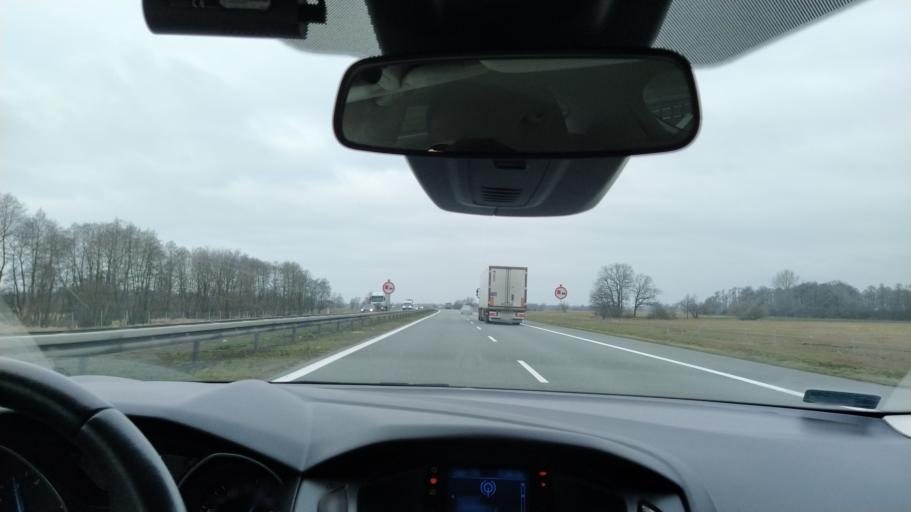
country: PL
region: Greater Poland Voivodeship
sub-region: Powiat koninski
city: Rzgow Pierwszy
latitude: 52.1892
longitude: 18.0792
